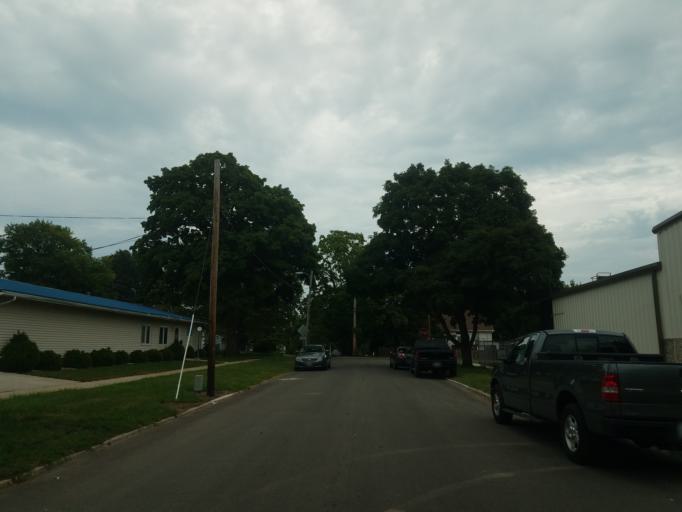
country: US
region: Illinois
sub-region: McLean County
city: Bloomington
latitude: 40.4859
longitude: -88.9823
